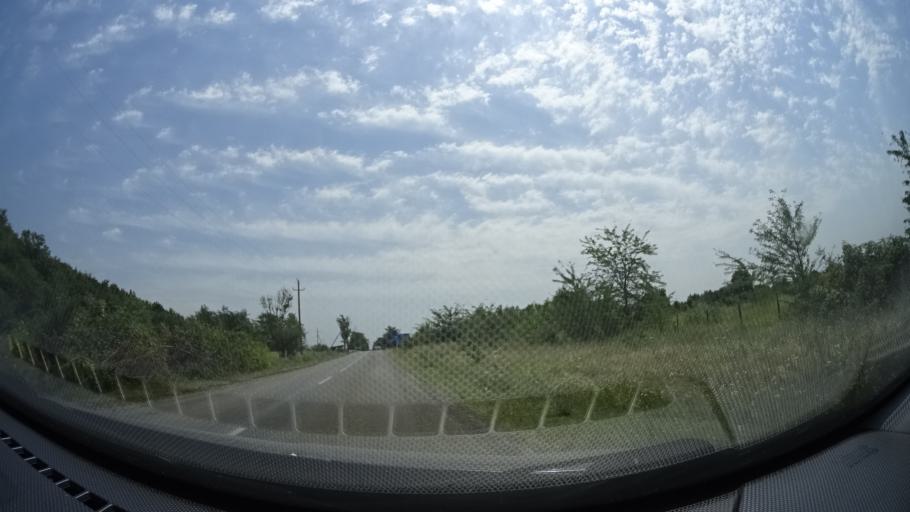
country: GE
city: Bagdadi
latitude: 41.8525
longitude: 46.0377
